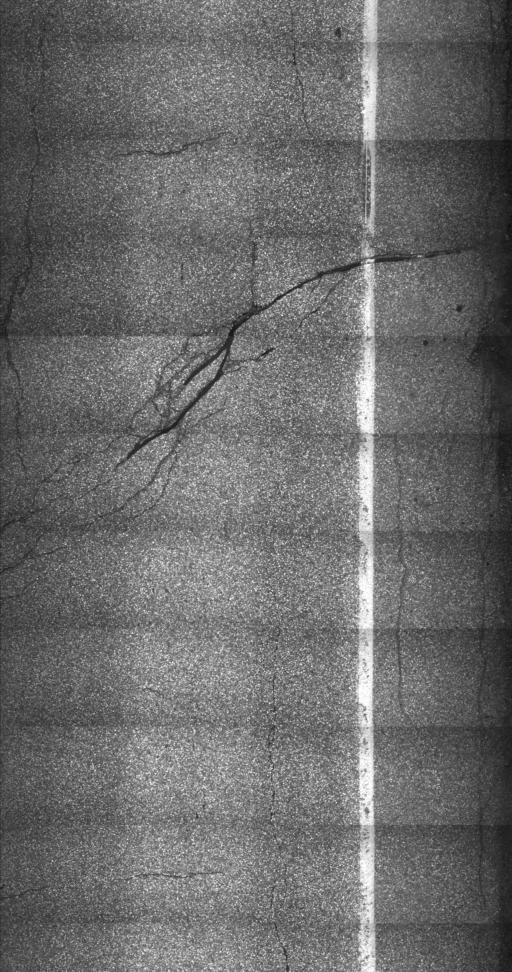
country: US
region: Vermont
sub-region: Orange County
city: Randolph
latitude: 43.7742
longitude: -72.8121
